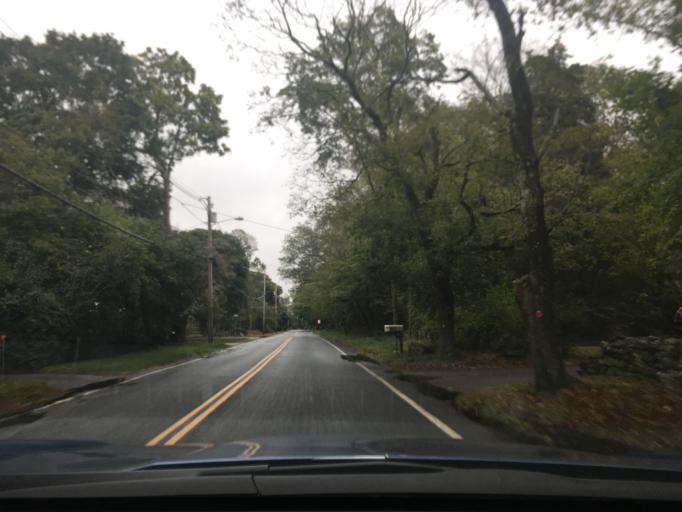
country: US
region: Rhode Island
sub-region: Kent County
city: East Greenwich
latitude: 41.6274
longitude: -71.4572
